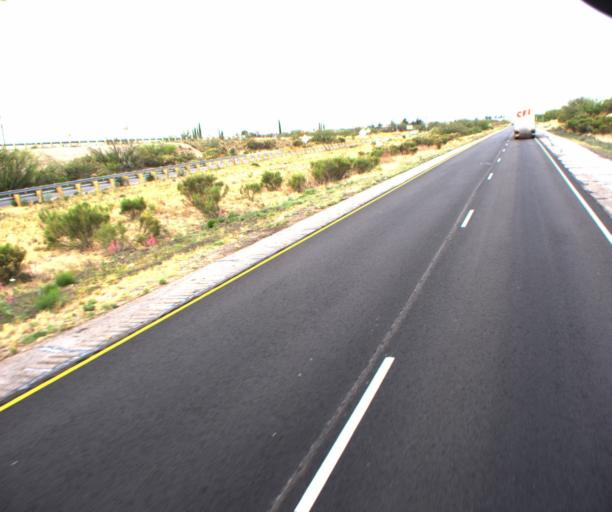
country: US
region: Arizona
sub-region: Cochise County
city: Mescal
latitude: 31.9631
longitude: -110.4347
